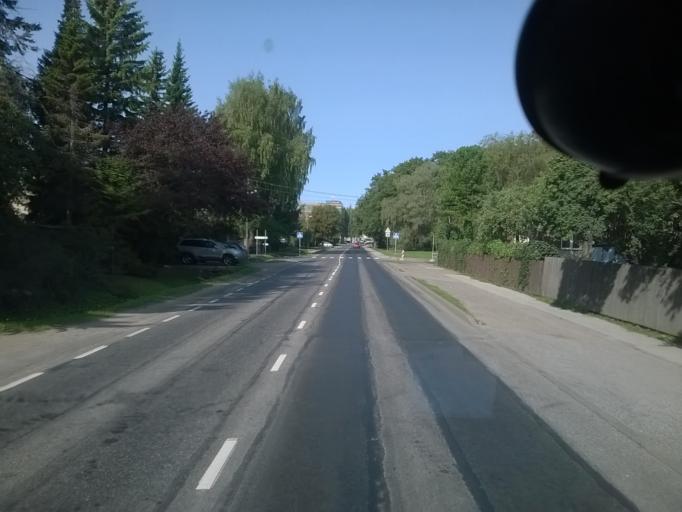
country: EE
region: Harju
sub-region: Tallinna linn
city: Tallinn
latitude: 59.4151
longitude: 24.6980
